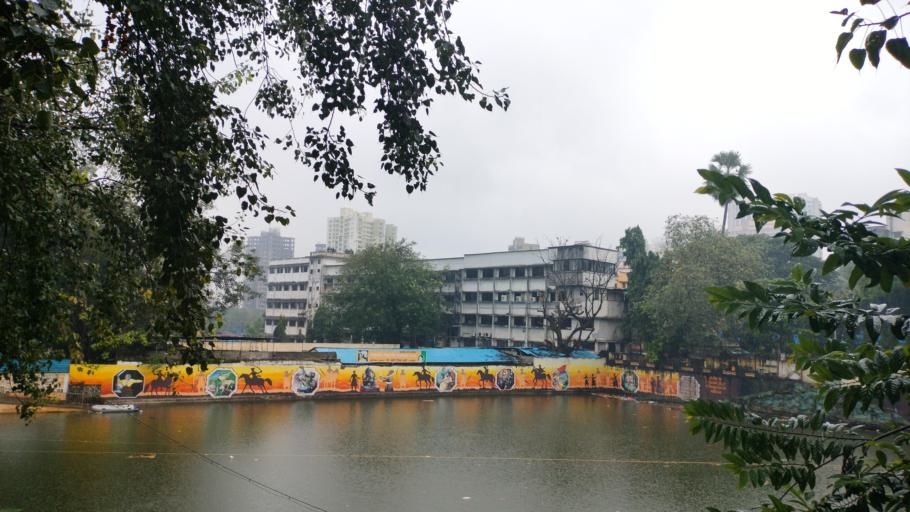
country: IN
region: Maharashtra
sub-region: Mumbai Suburban
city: Powai
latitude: 19.1477
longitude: 72.9298
